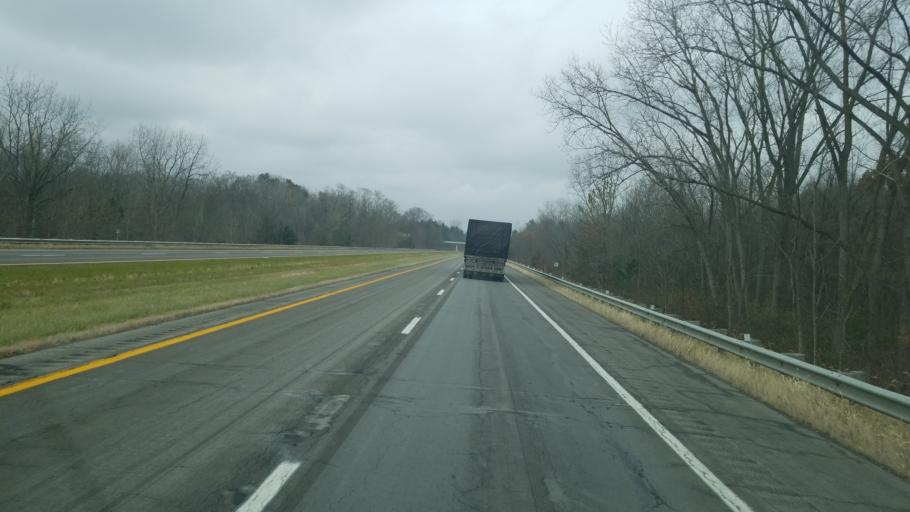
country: US
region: Ohio
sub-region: Huron County
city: Norwalk
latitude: 41.2233
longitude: -82.6257
